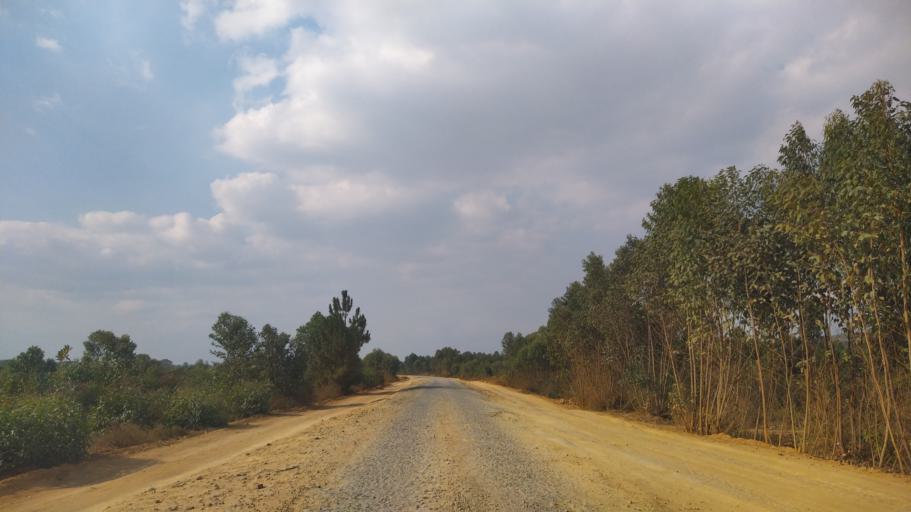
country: MG
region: Alaotra Mangoro
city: Moramanga
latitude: -18.6453
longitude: 48.2753
